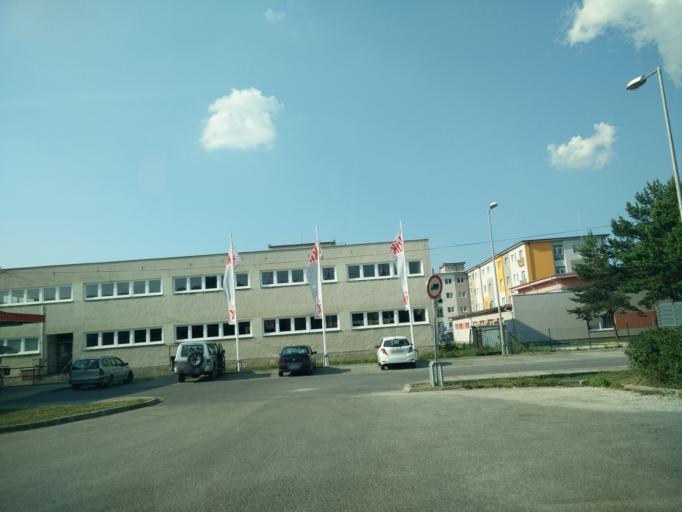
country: SK
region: Zilinsky
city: Rajec
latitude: 49.0930
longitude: 18.6382
